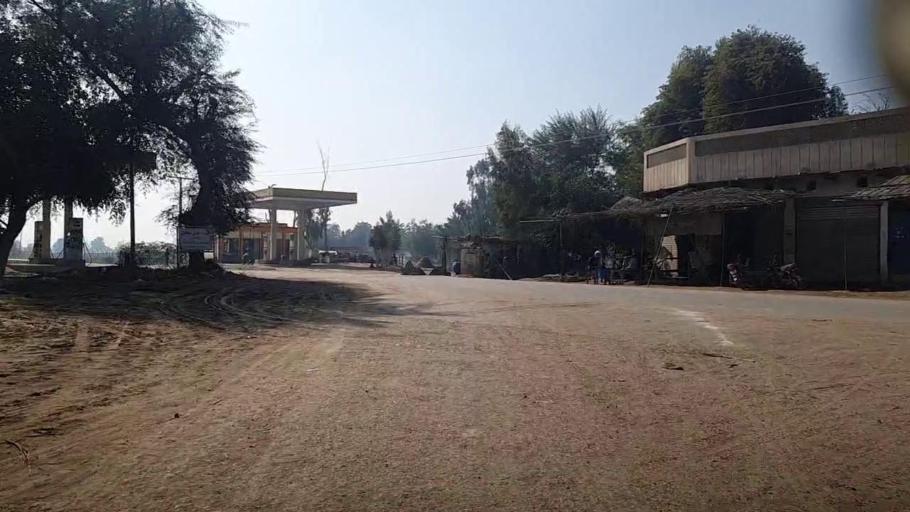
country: PK
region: Sindh
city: Khairpur
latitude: 27.9405
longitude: 69.6700
